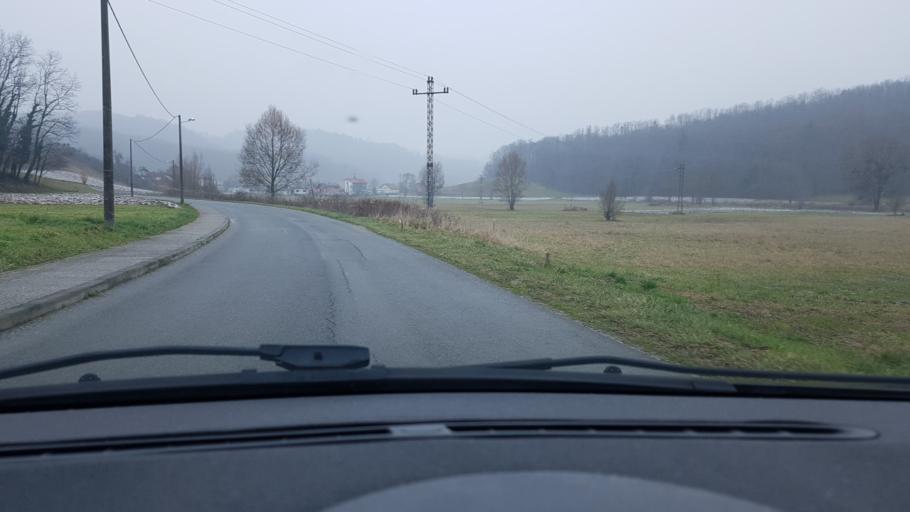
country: HR
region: Krapinsko-Zagorska
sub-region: Grad Krapina
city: Krapina
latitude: 46.1169
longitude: 15.8752
